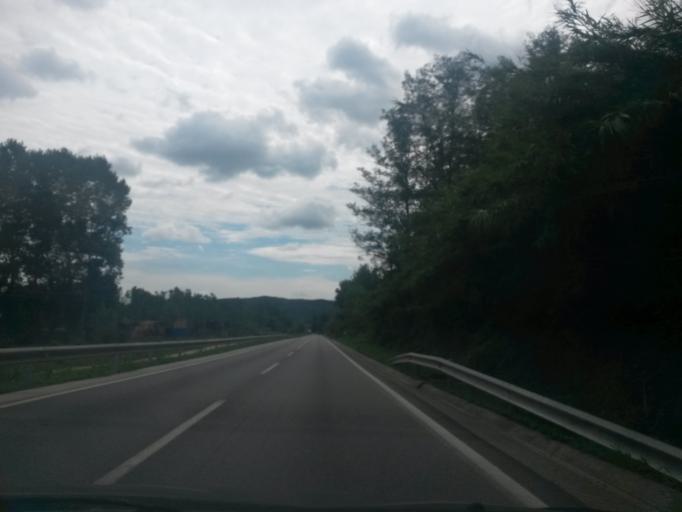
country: ES
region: Catalonia
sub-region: Provincia de Girona
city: Sant Gregori
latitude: 41.9716
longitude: 2.7164
